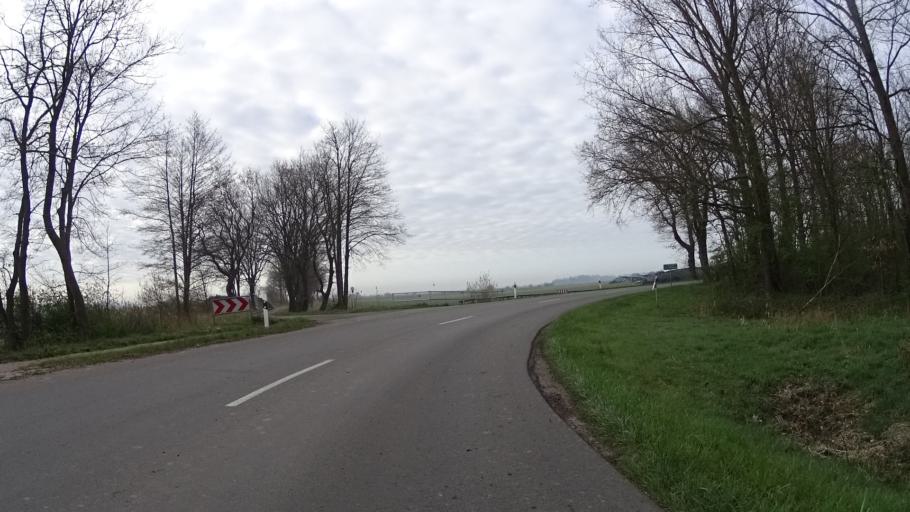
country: DE
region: Lower Saxony
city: Upgant-Schott
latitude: 53.4431
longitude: 7.3313
